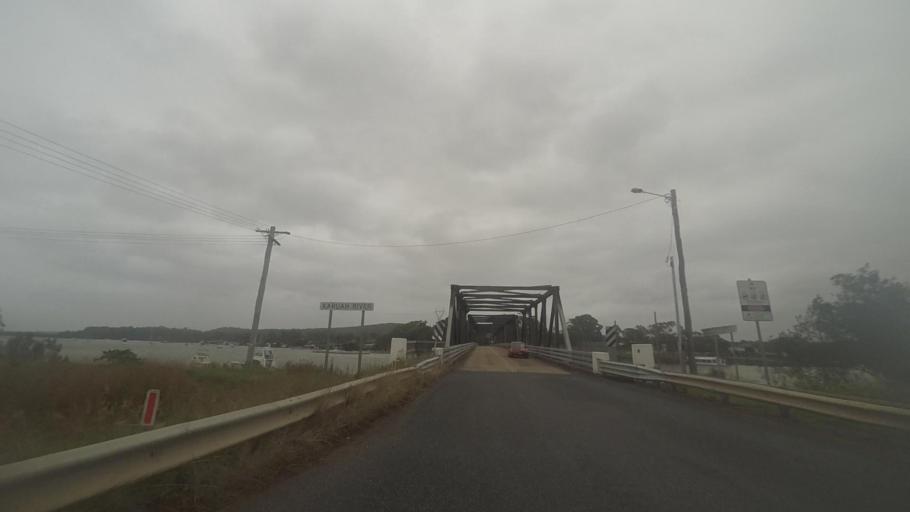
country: AU
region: New South Wales
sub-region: Port Stephens Shire
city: Port Stephens
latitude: -32.6537
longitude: 151.9702
